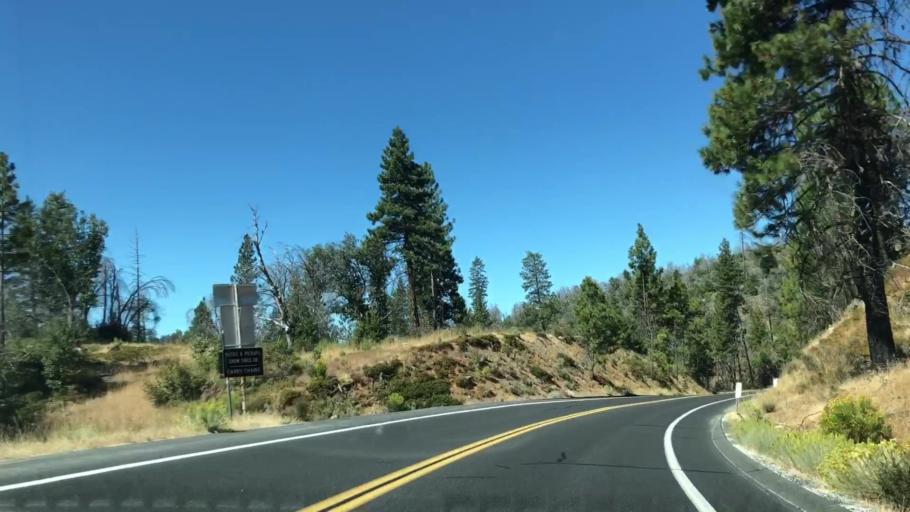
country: US
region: California
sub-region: Mariposa County
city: Midpines
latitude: 37.8163
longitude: -119.9292
